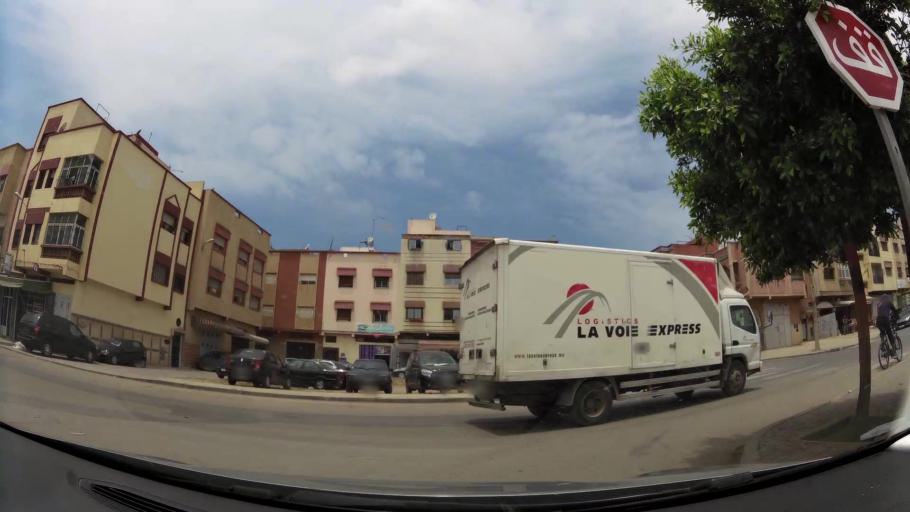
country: MA
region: Rabat-Sale-Zemmour-Zaer
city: Sale
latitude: 34.0571
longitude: -6.7857
